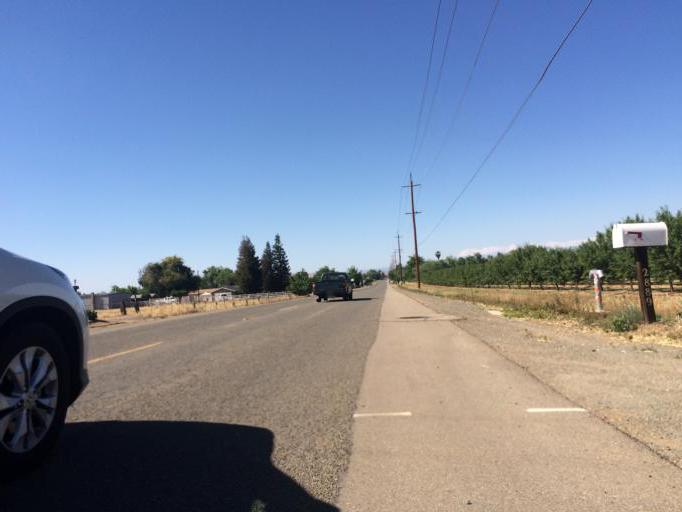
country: US
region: California
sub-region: Fresno County
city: Sanger
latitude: 36.7768
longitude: -119.6101
